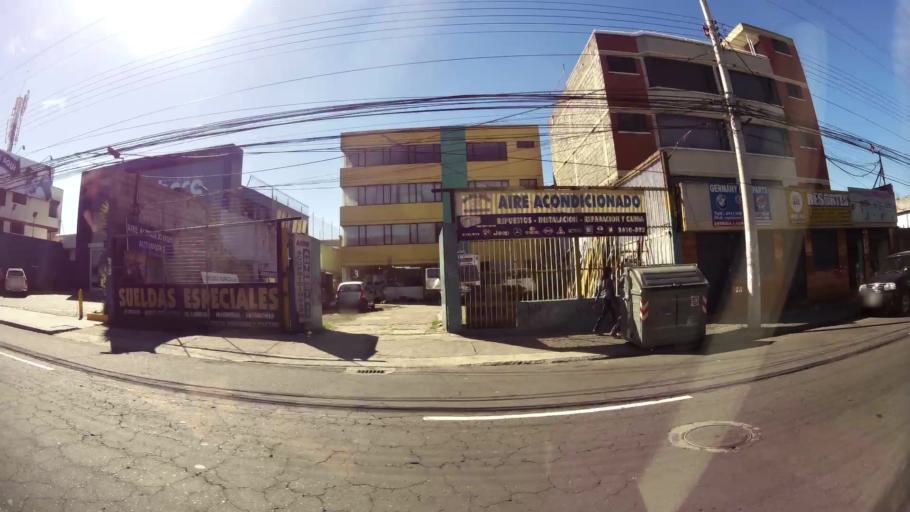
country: EC
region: Pichincha
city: Quito
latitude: -0.1504
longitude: -78.4760
